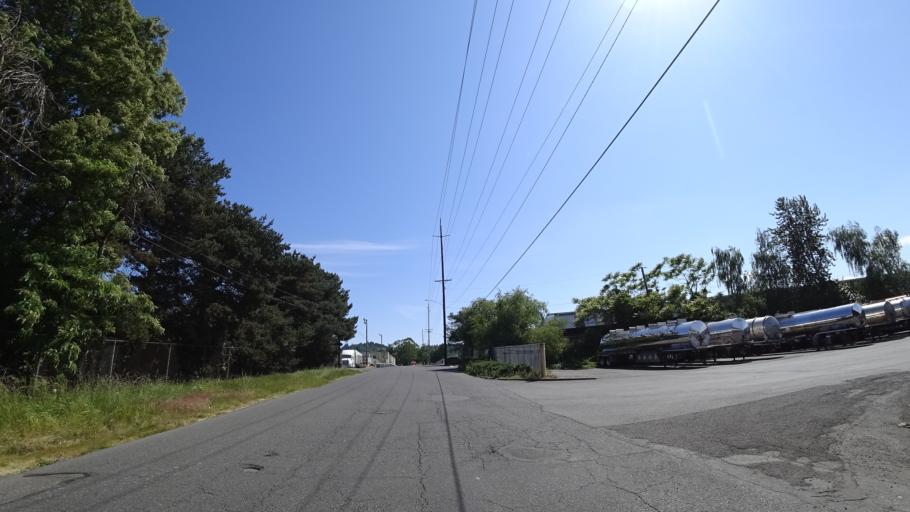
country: US
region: Oregon
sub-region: Multnomah County
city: Lents
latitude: 45.5653
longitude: -122.5684
